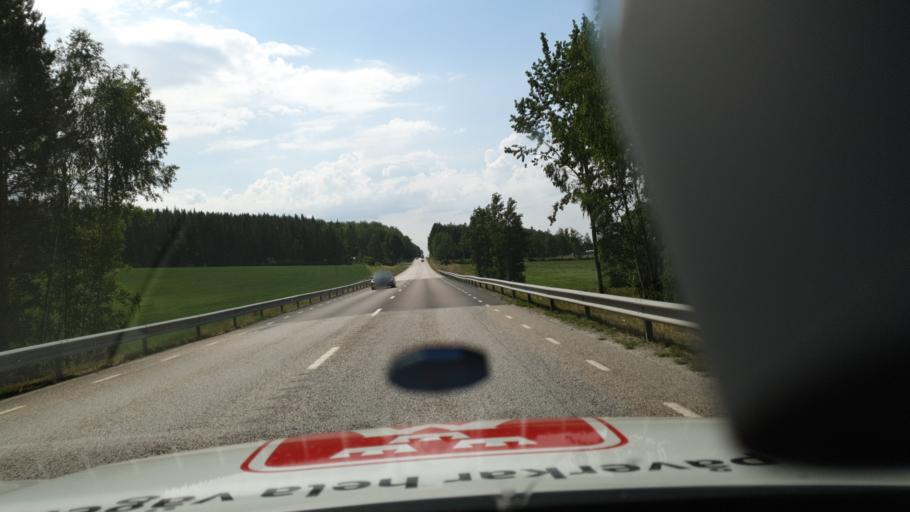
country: SE
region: Joenkoeping
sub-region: Habo Kommun
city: Habo
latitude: 57.9113
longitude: 14.1022
